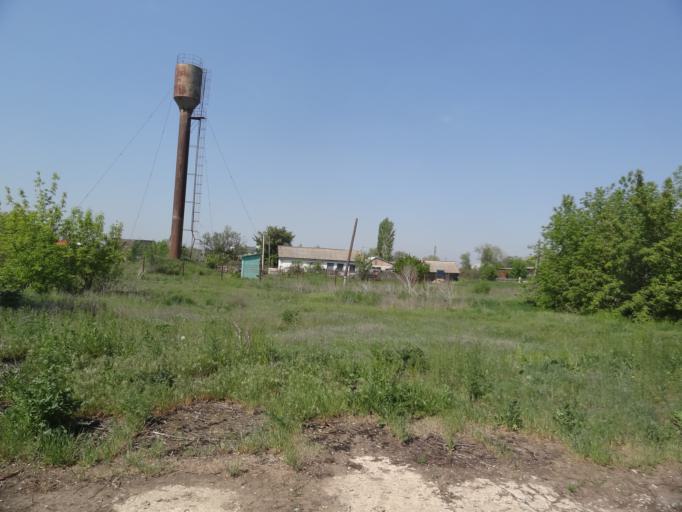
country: RU
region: Saratov
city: Privolzhskiy
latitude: 51.4075
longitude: 46.1054
